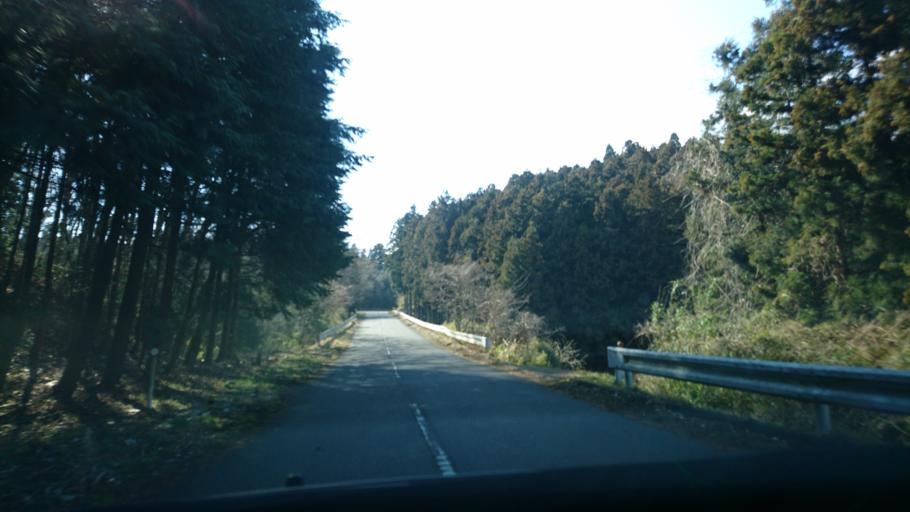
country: JP
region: Iwate
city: Ichinoseki
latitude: 38.8078
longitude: 141.2106
